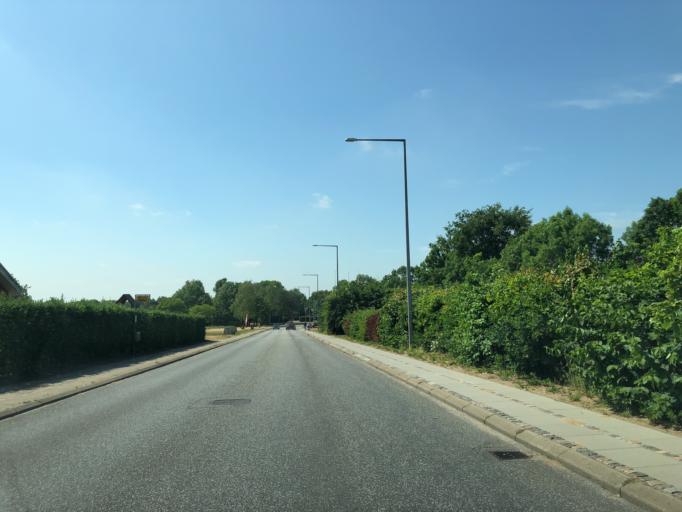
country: DK
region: South Denmark
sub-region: Kolding Kommune
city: Kolding
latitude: 55.5202
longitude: 9.4791
